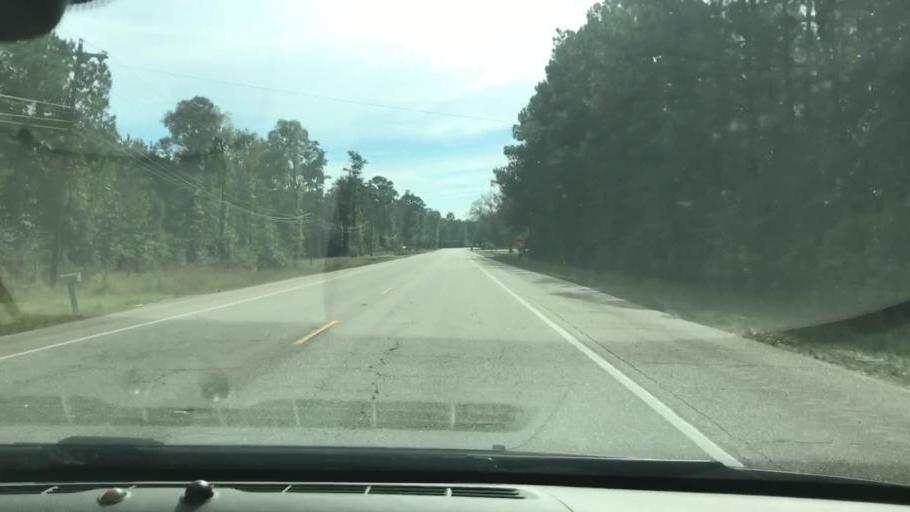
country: US
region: Mississippi
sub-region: Pearl River County
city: Nicholson
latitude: 30.5047
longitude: -89.8173
